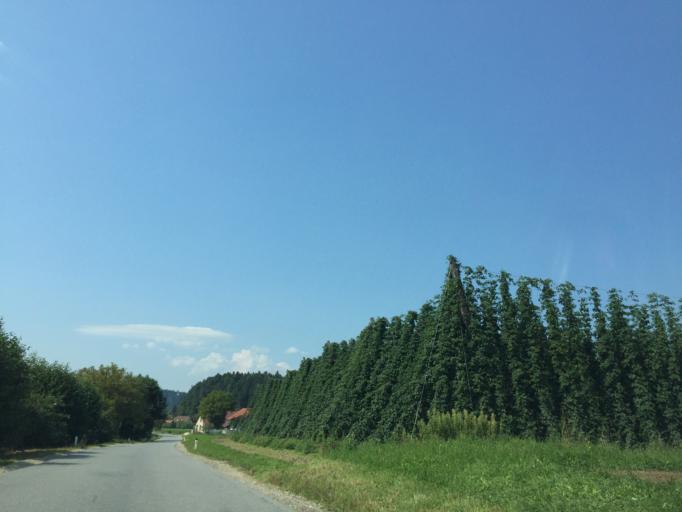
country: SI
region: Slovenj Gradec
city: Slovenj Gradec
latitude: 46.4837
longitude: 15.0789
